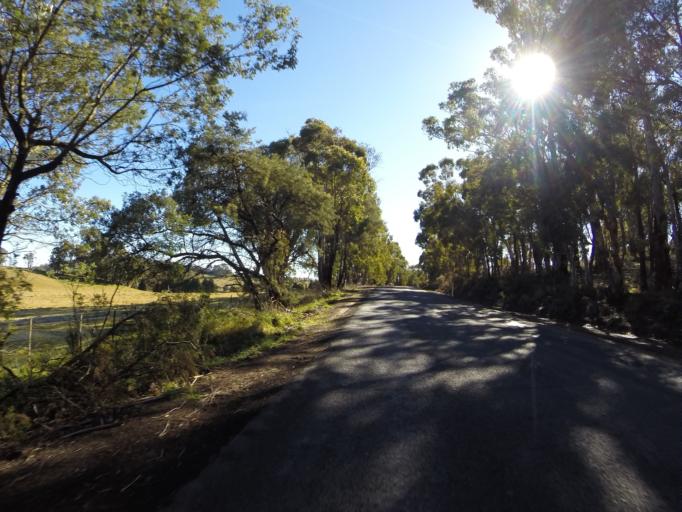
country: AU
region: New South Wales
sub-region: Oberon
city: Oberon
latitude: -33.6333
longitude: 149.8452
